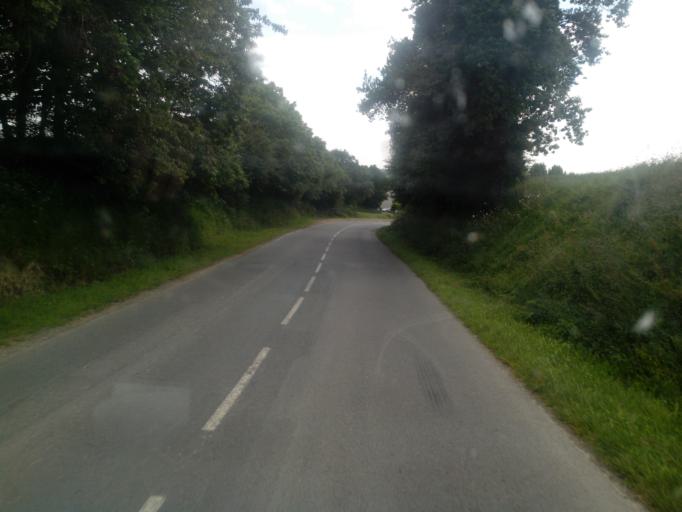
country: FR
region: Brittany
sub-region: Departement d'Ille-et-Vilaine
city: Montreuil-sur-Ille
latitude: 48.3217
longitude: -1.6465
